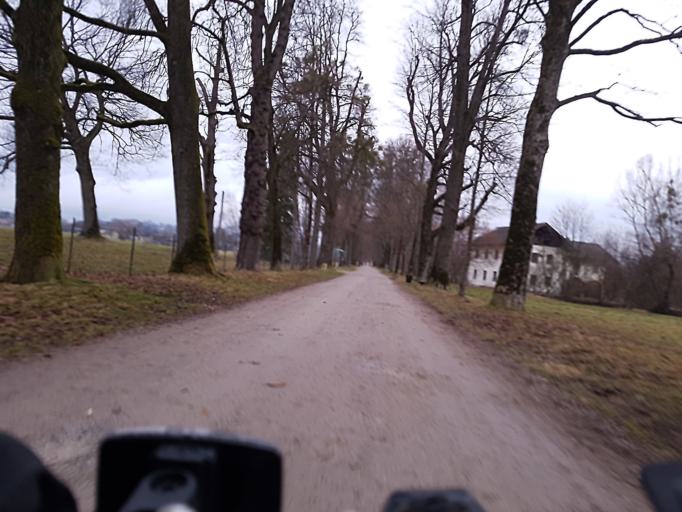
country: AT
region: Salzburg
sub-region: Politischer Bezirk Salzburg-Umgebung
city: Anif
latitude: 47.7731
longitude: 13.0617
